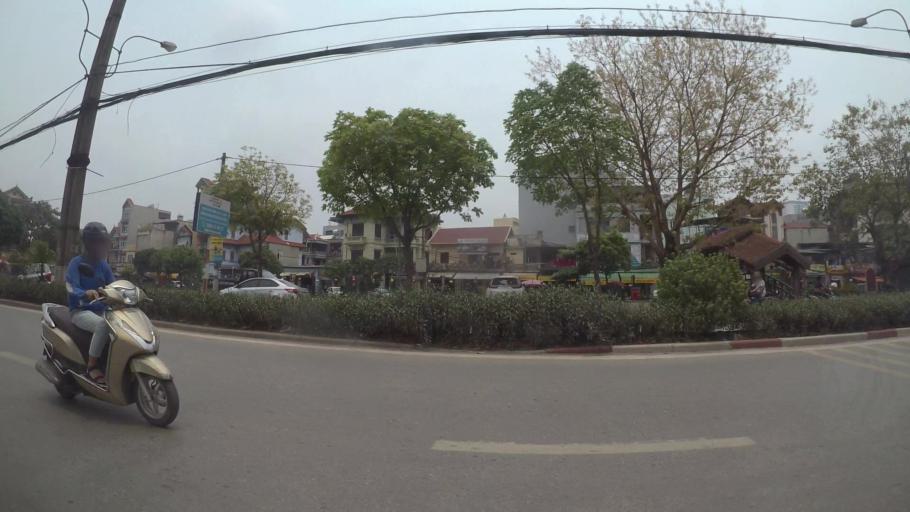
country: VN
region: Ha Noi
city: Ha Dong
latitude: 20.9771
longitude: 105.7756
